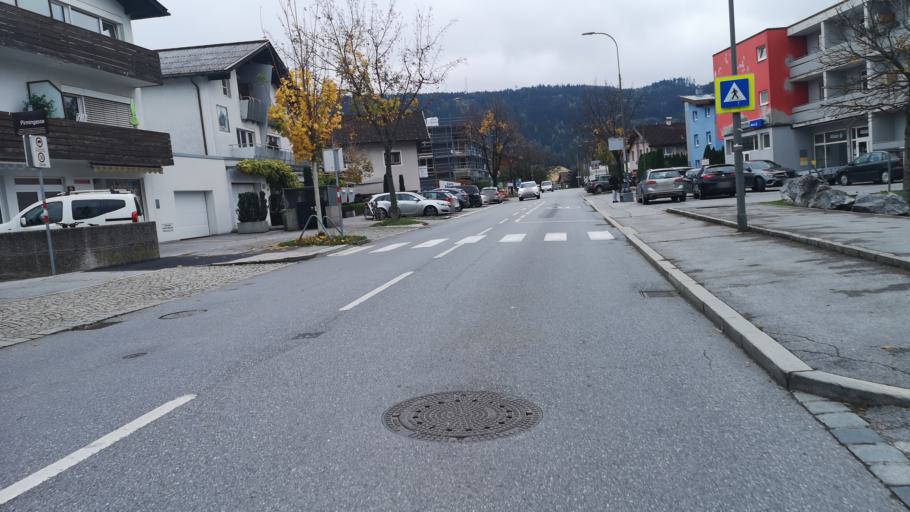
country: AT
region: Tyrol
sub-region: Politischer Bezirk Innsbruck Land
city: Natters
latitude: 47.2620
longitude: 11.3651
